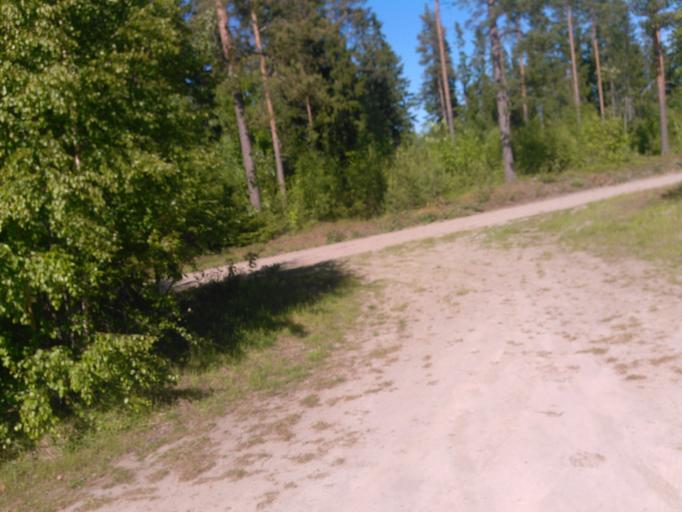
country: SE
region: Vaesterbotten
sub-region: Umea Kommun
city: Roback
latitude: 63.8262
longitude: 20.1742
